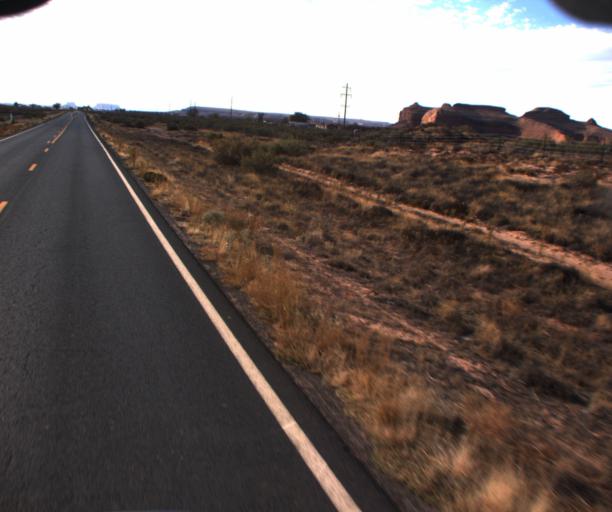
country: US
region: Arizona
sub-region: Apache County
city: Many Farms
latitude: 36.7308
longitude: -109.6320
